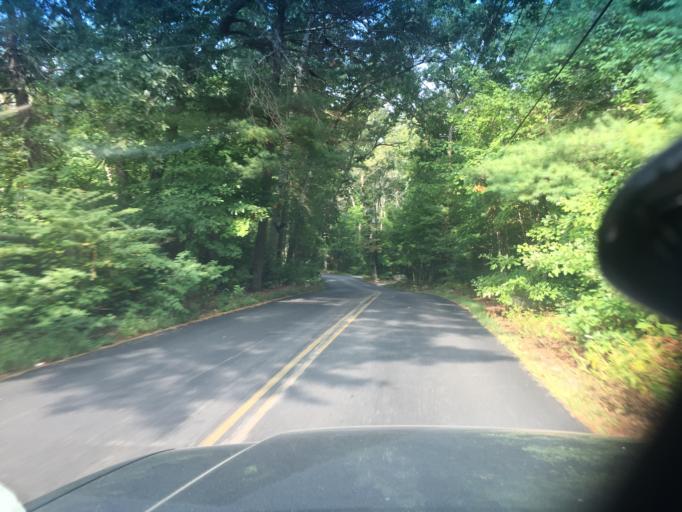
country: US
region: Massachusetts
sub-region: Norfolk County
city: Bellingham
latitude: 42.1319
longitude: -71.4625
